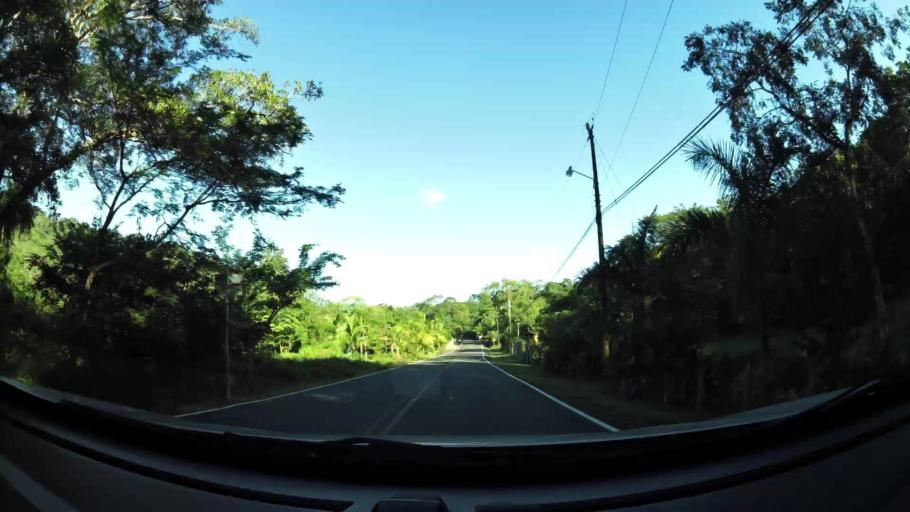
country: CR
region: Guanacaste
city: Juntas
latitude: 10.2018
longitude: -84.8452
